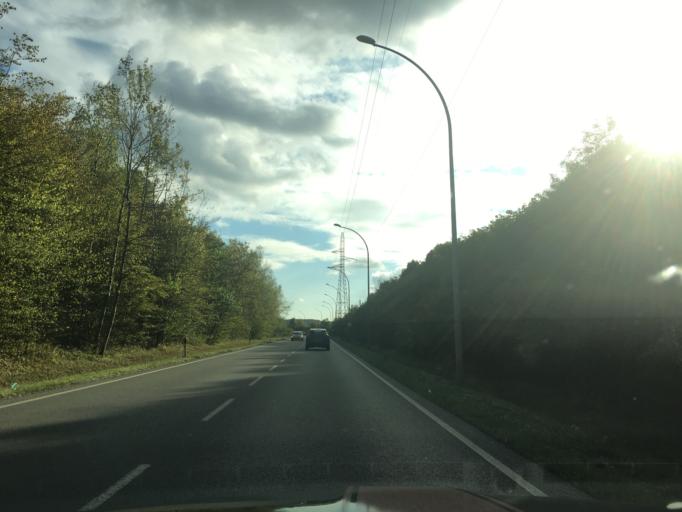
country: LU
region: Luxembourg
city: Belvaux
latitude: 49.5271
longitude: 5.9243
